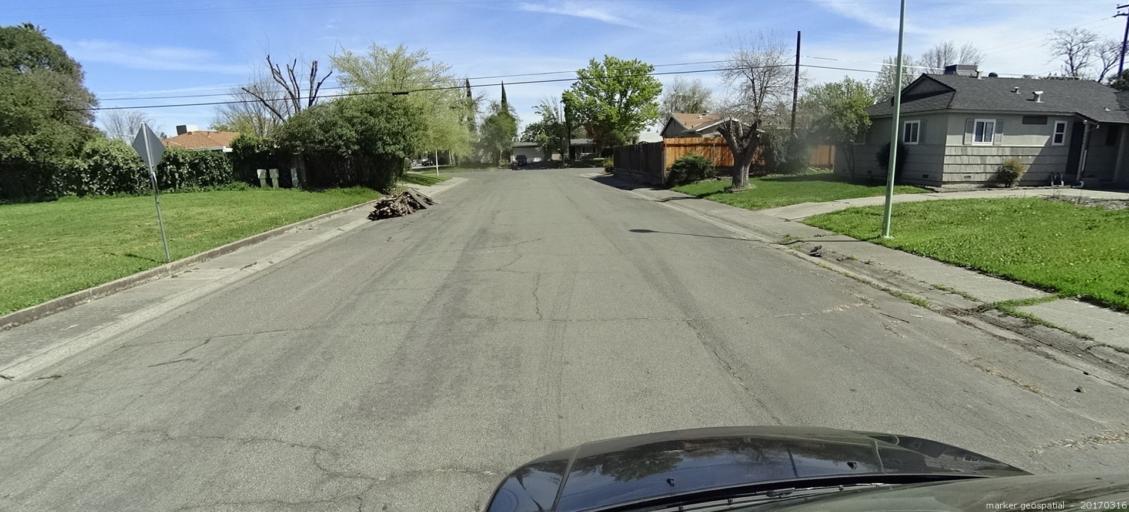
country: US
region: California
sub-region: Sacramento County
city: Parkway
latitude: 38.4788
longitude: -121.4925
